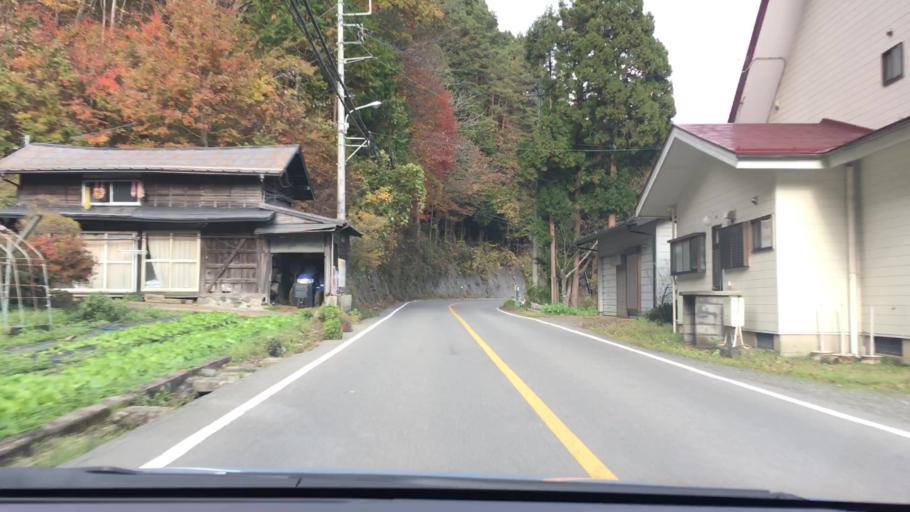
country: JP
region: Yamanashi
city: Otsuki
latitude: 35.4851
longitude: 138.9622
